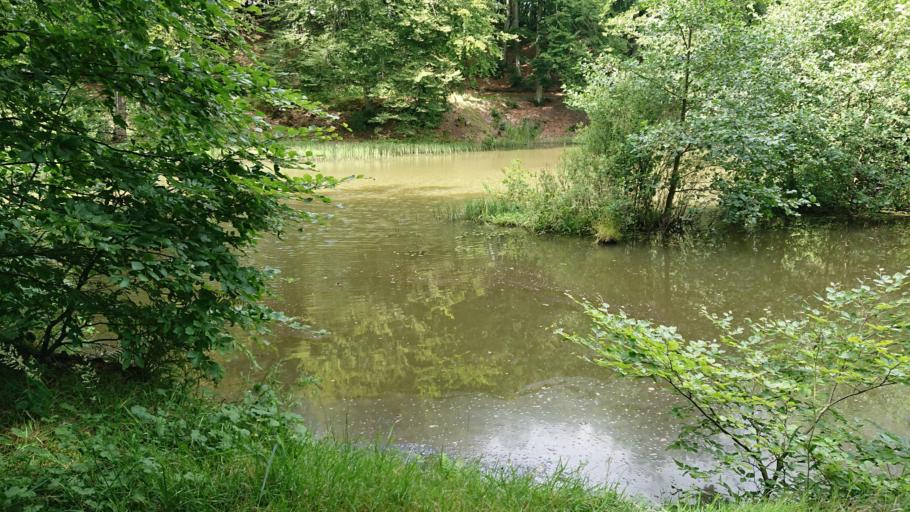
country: DK
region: North Denmark
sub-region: Hjorring Kommune
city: Sindal
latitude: 57.4501
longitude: 10.3342
